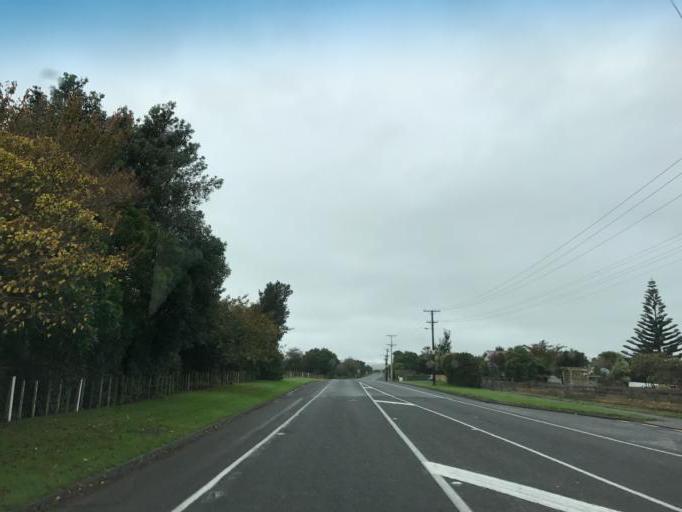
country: NZ
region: Taranaki
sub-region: South Taranaki District
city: Patea
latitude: -39.7638
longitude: 174.6356
